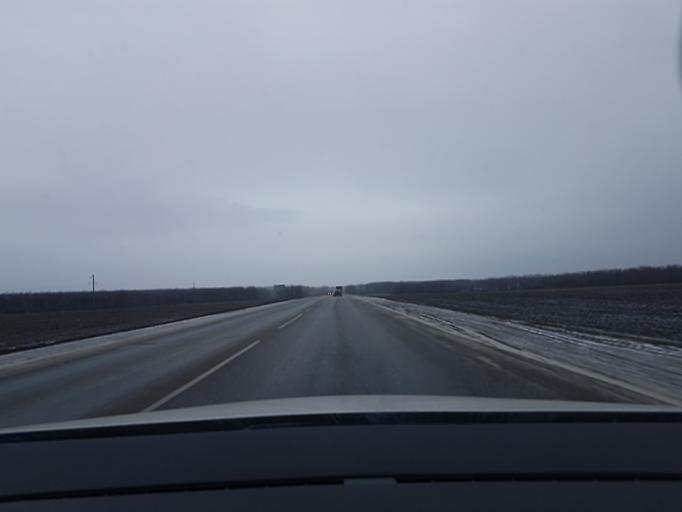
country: RU
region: Tambov
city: Zavoronezhskoye
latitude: 52.9911
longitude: 40.5551
